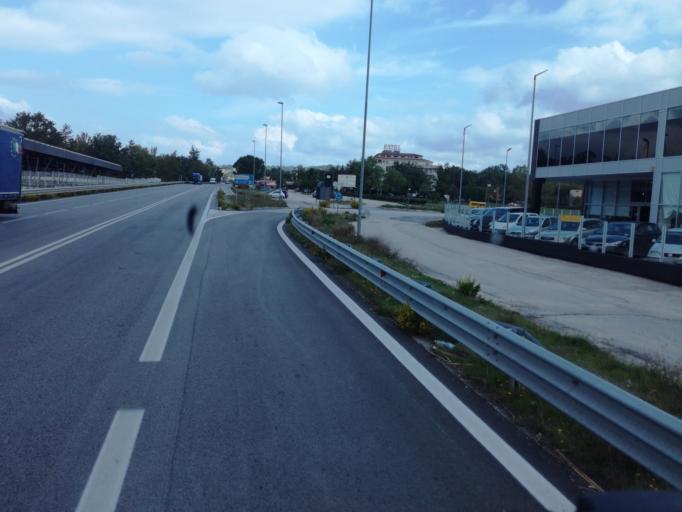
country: IT
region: Molise
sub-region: Provincia di Campobasso
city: Guardiaregia
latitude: 41.4689
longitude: 14.5591
